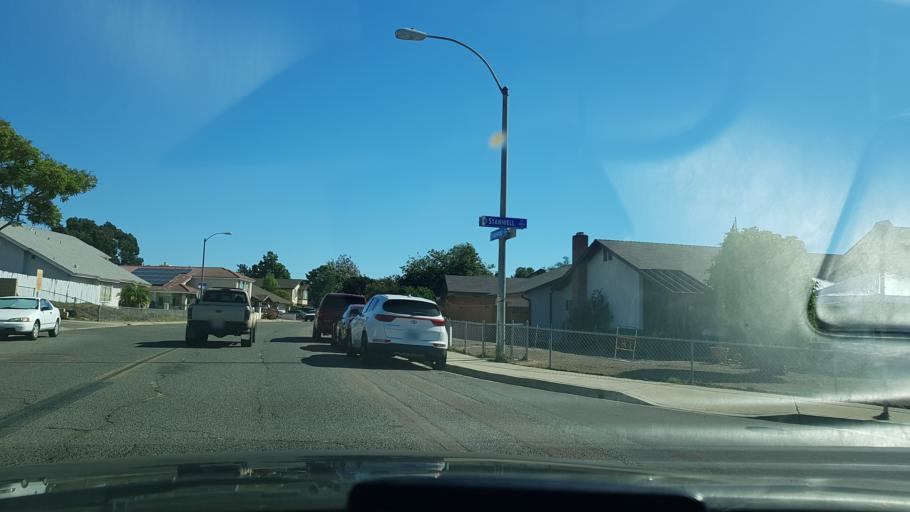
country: US
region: California
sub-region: San Diego County
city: Fairbanks Ranch
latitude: 32.9133
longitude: -117.1323
